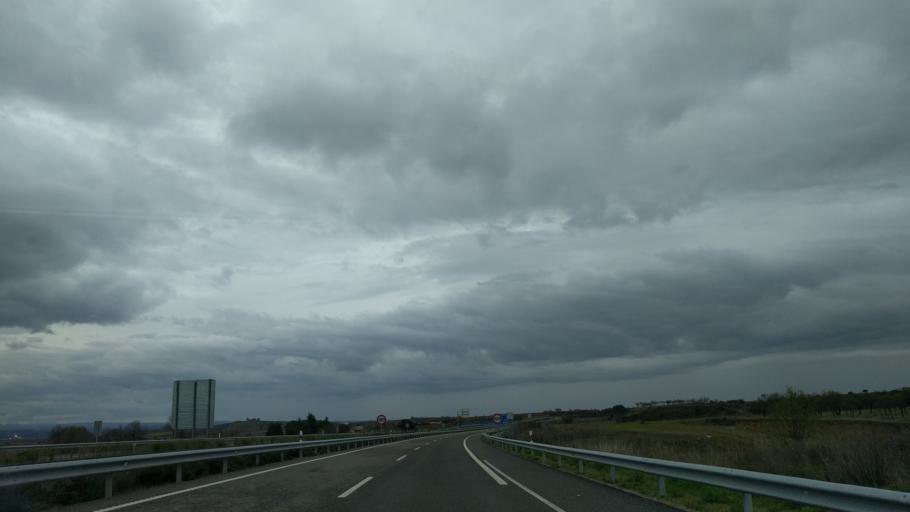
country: ES
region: Aragon
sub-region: Provincia de Huesca
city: Barbastro
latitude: 41.9976
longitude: 0.1015
